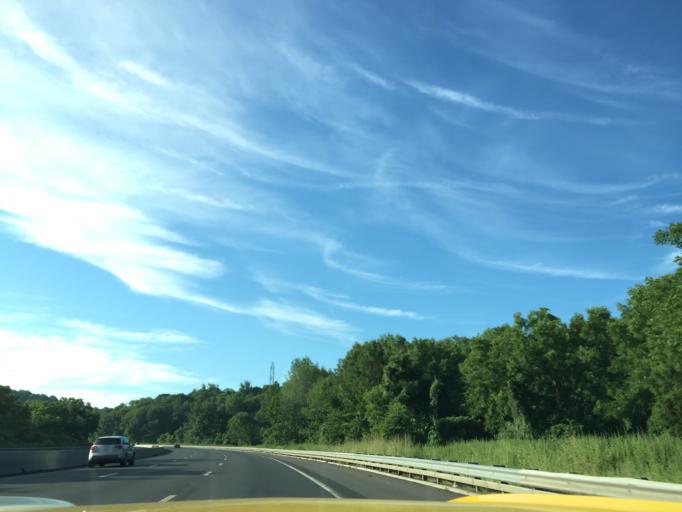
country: US
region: New Jersey
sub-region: Hunterdon County
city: Hampton
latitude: 40.6549
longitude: -75.0390
